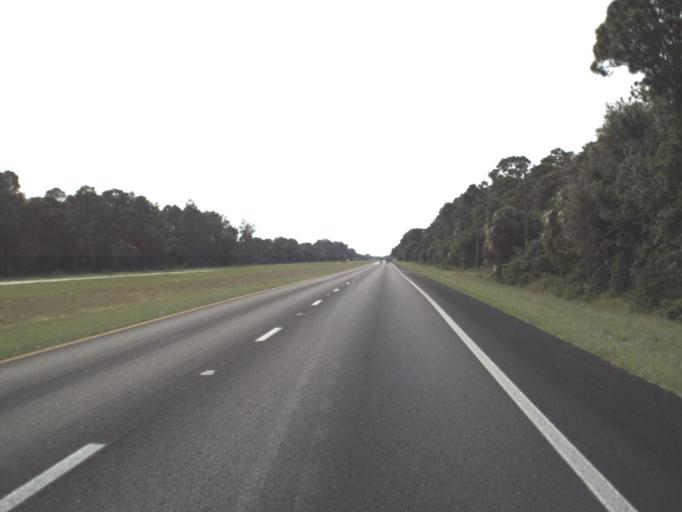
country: US
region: Florida
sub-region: Hendry County
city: Port LaBelle
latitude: 26.7686
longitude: -81.3488
